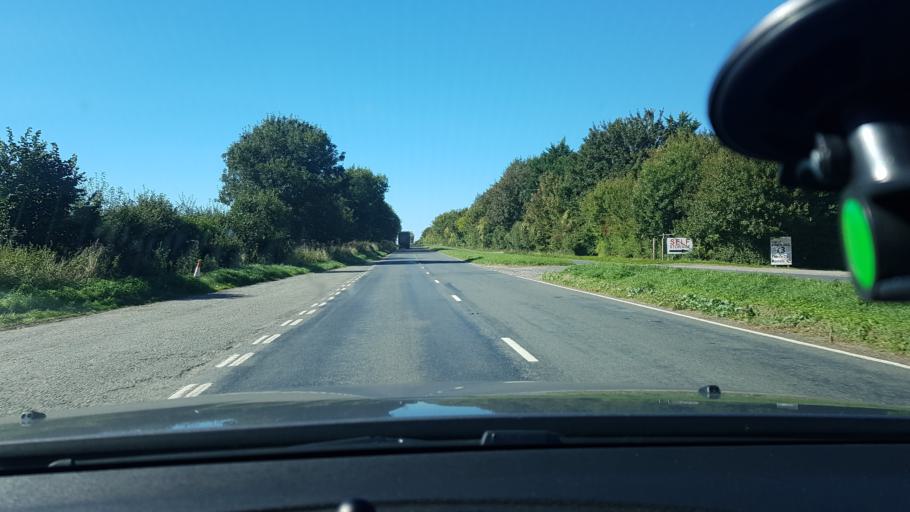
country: GB
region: England
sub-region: Hampshire
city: Kings Worthy
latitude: 51.0615
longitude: -1.2456
